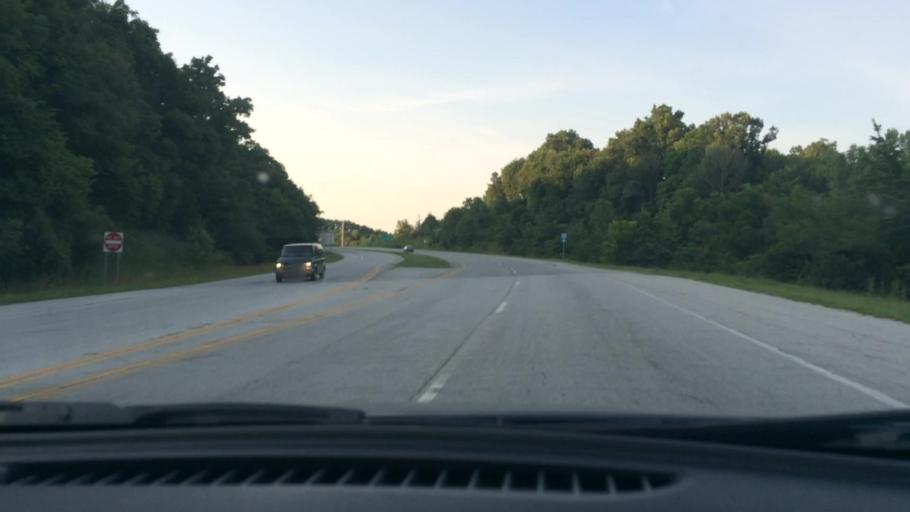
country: US
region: Indiana
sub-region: Tippecanoe County
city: Battle Ground
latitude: 40.4923
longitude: -86.8692
